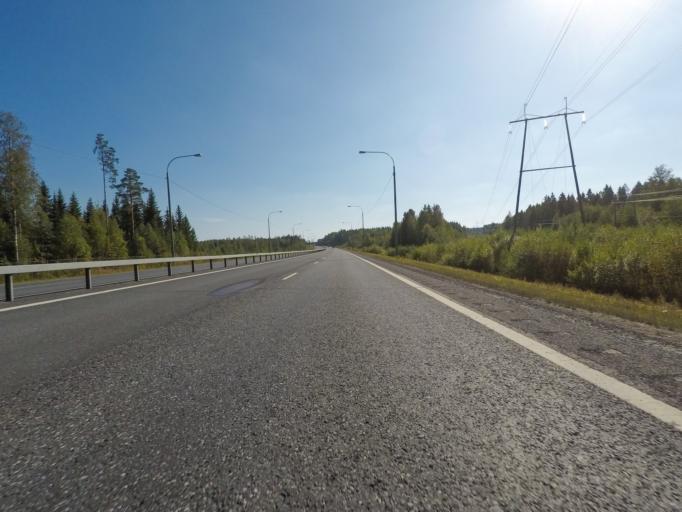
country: FI
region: Northern Savo
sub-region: Kuopio
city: Kuopio
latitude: 62.7516
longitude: 27.5809
